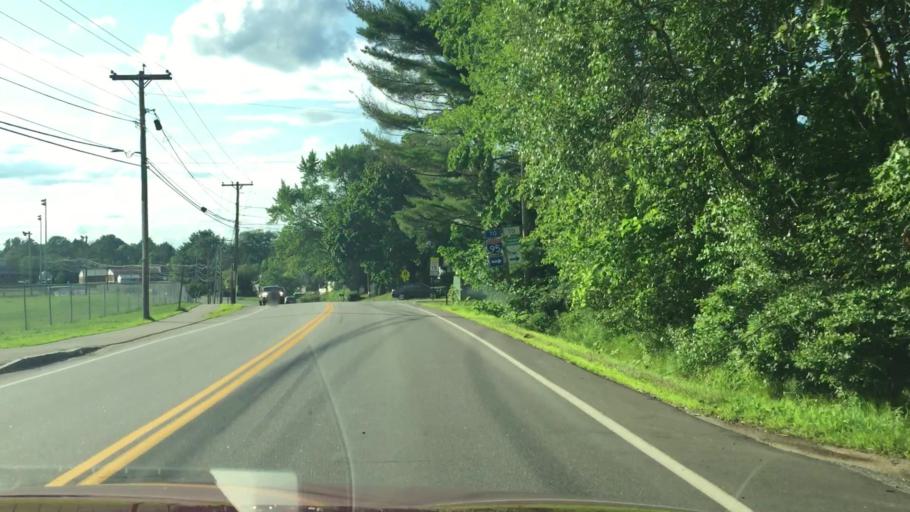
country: US
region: Maine
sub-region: Cumberland County
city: Westbrook
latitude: 43.6715
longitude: -70.3496
